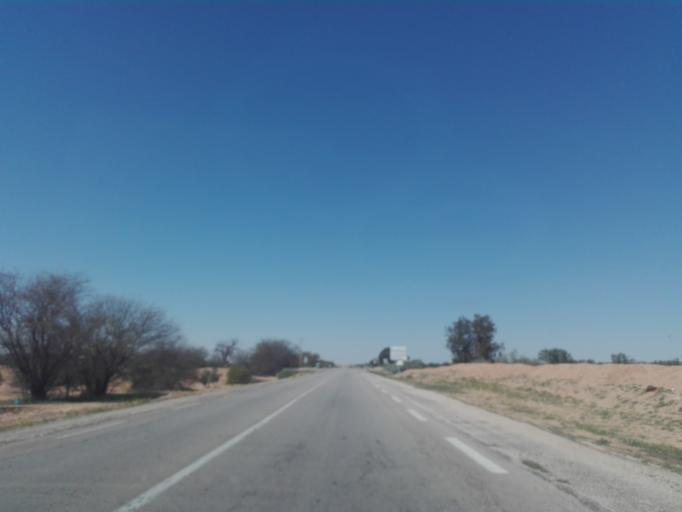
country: TN
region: Safaqis
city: Bi'r `Ali Bin Khalifah
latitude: 34.7574
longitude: 10.2725
